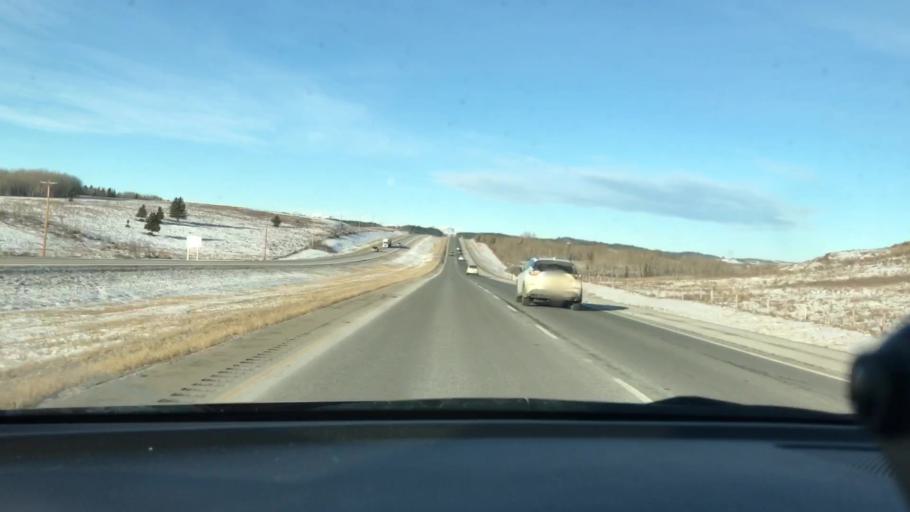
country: CA
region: Alberta
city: Cochrane
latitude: 51.1172
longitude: -114.6590
